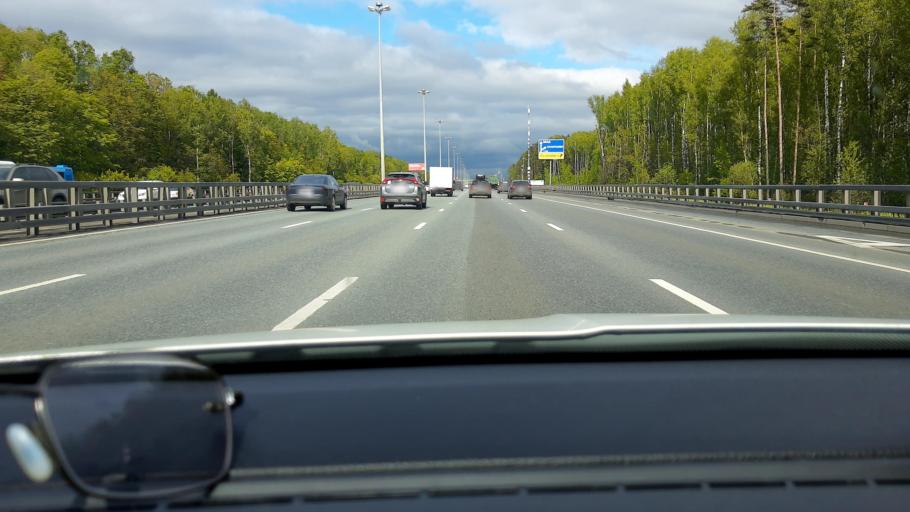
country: RU
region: Moscow
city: Solntsevo
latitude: 55.6210
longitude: 37.4022
